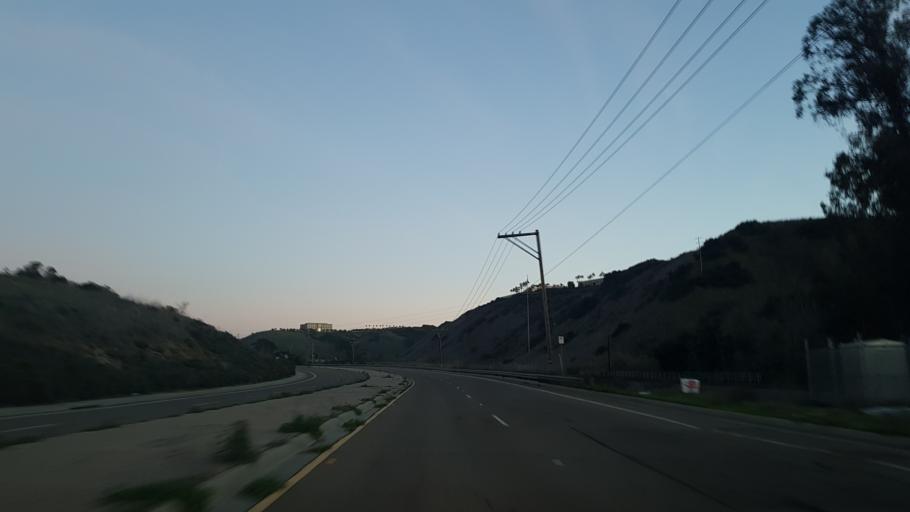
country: US
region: California
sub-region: San Diego County
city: La Jolla
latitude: 32.8942
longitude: -117.2165
